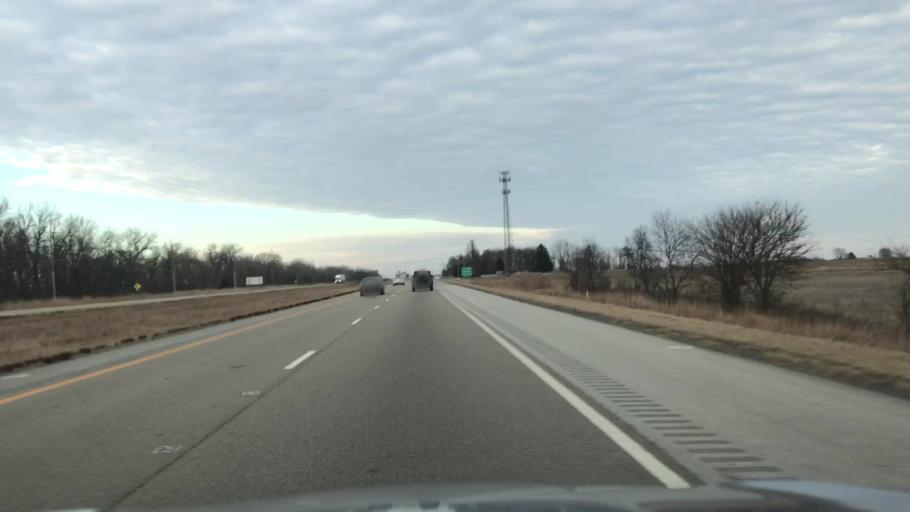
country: US
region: Illinois
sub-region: Logan County
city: Atlanta
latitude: 40.2348
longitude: -89.2616
